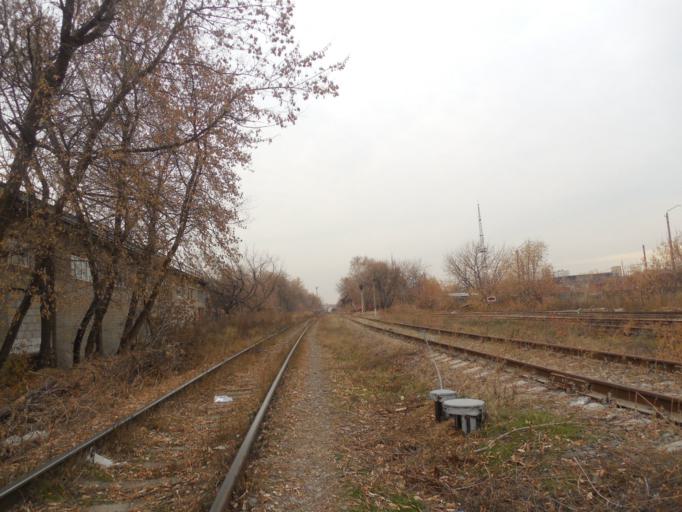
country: RU
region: Moscow
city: Lefortovo
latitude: 55.7393
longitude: 37.7132
